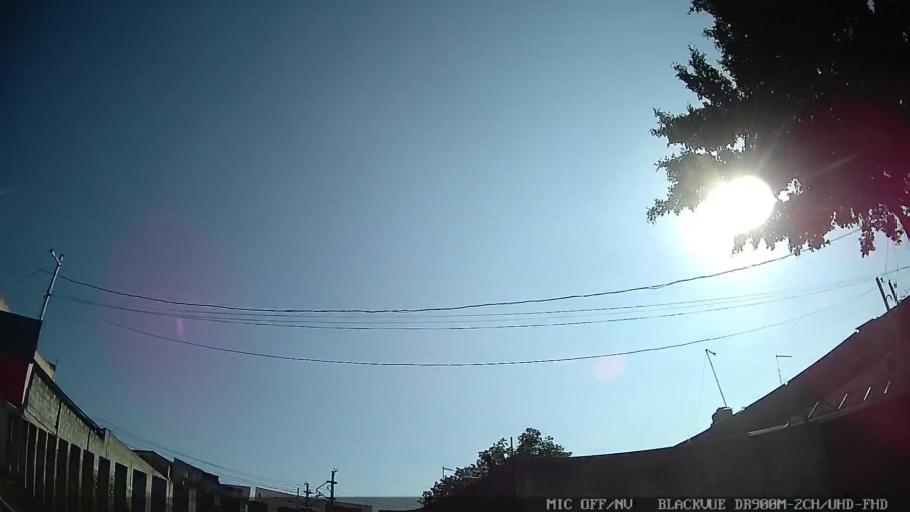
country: BR
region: Sao Paulo
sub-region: Ferraz De Vasconcelos
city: Ferraz de Vasconcelos
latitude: -23.5386
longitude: -46.4241
